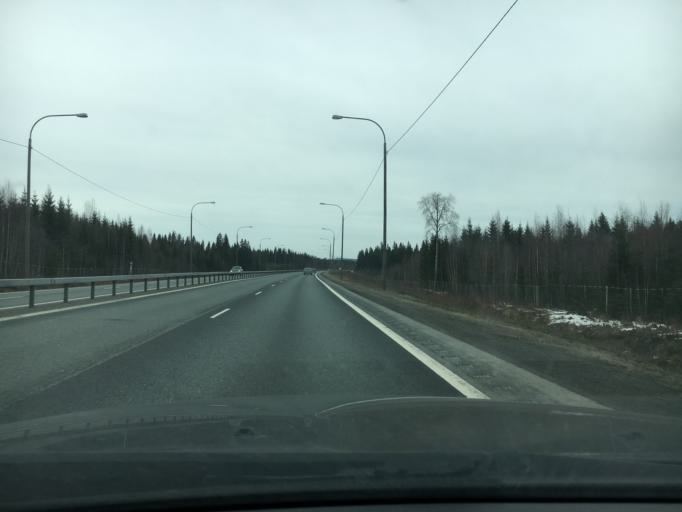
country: FI
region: Northern Savo
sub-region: Kuopio
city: Kuopio
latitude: 62.7645
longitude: 27.5817
